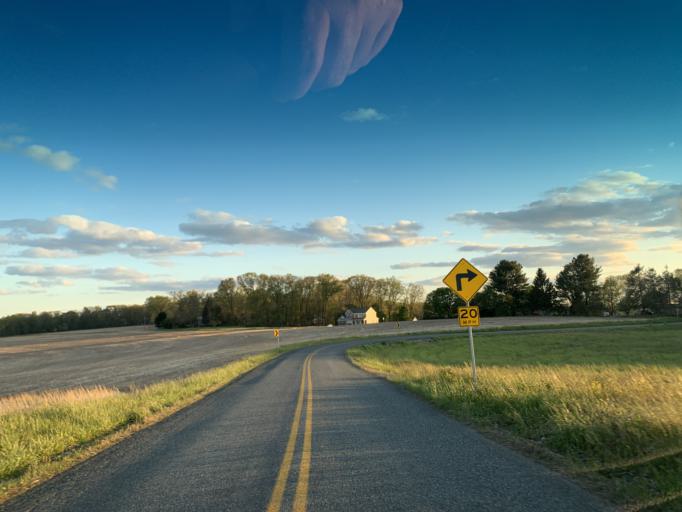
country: US
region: Maryland
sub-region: Harford County
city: Jarrettsville
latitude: 39.6591
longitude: -76.4145
